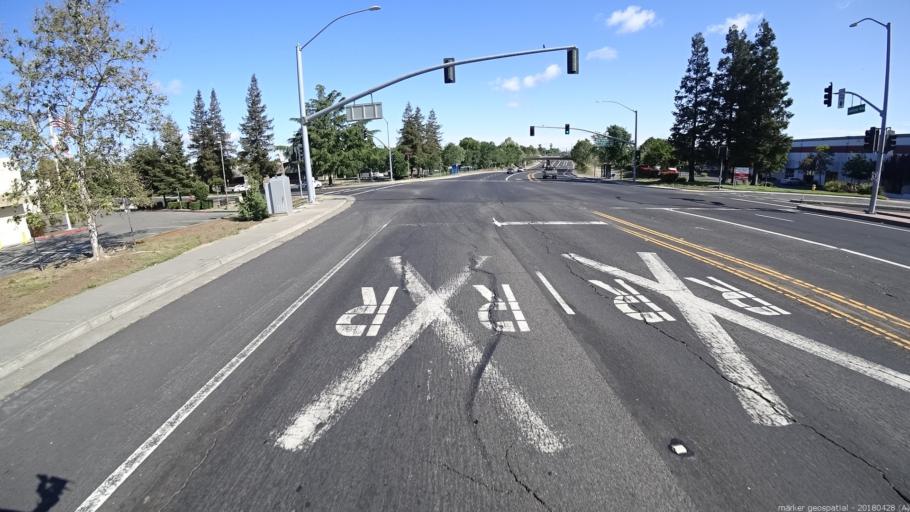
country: US
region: California
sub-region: Yolo County
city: West Sacramento
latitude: 38.5865
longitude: -121.5269
